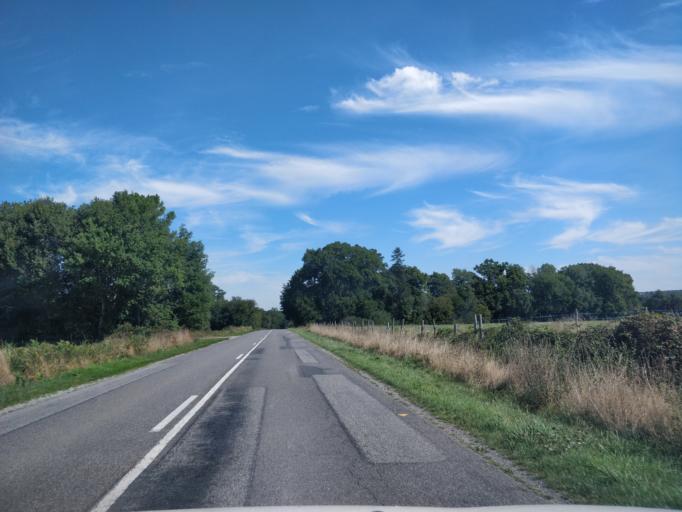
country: FR
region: Pays de la Loire
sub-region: Departement de la Loire-Atlantique
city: Guemene-Penfao
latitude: 47.6168
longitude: -1.8372
